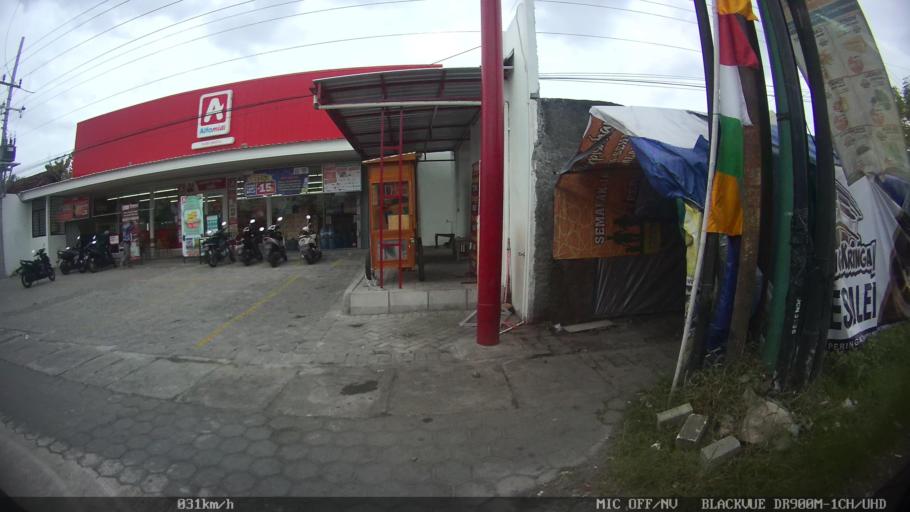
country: ID
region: Daerah Istimewa Yogyakarta
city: Sewon
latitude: -7.8331
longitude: 110.4124
